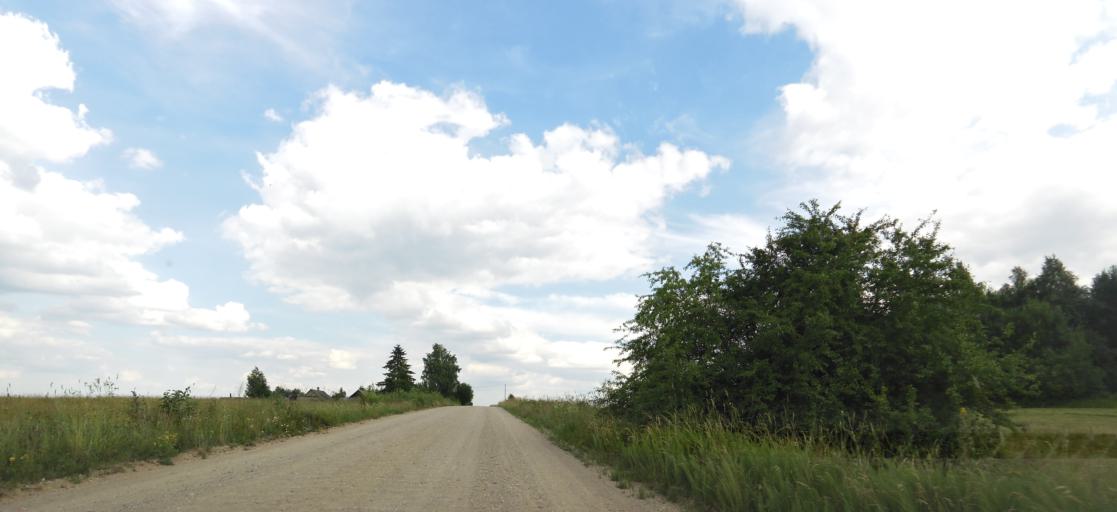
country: LT
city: Skaidiskes
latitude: 54.5311
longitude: 25.6339
